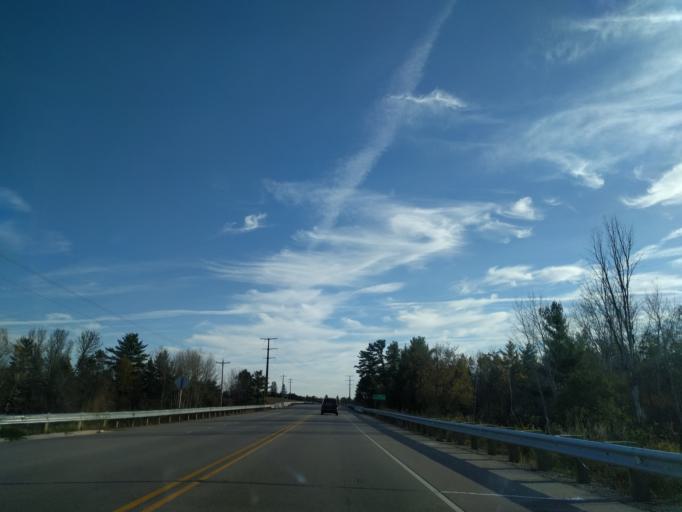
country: US
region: Wisconsin
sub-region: Marinette County
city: Peshtigo
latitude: 45.2871
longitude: -87.9917
